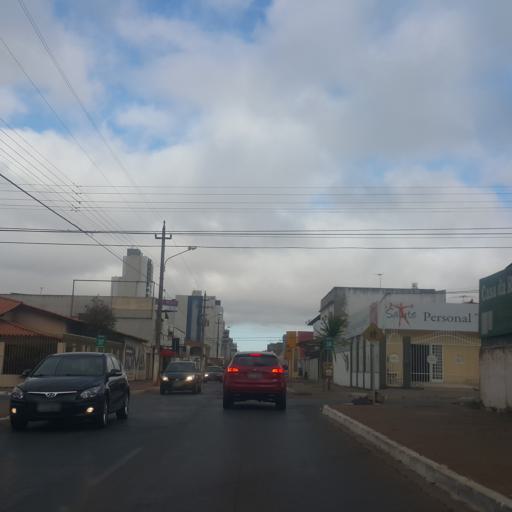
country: BR
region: Federal District
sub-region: Brasilia
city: Brasilia
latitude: -15.8221
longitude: -48.0576
